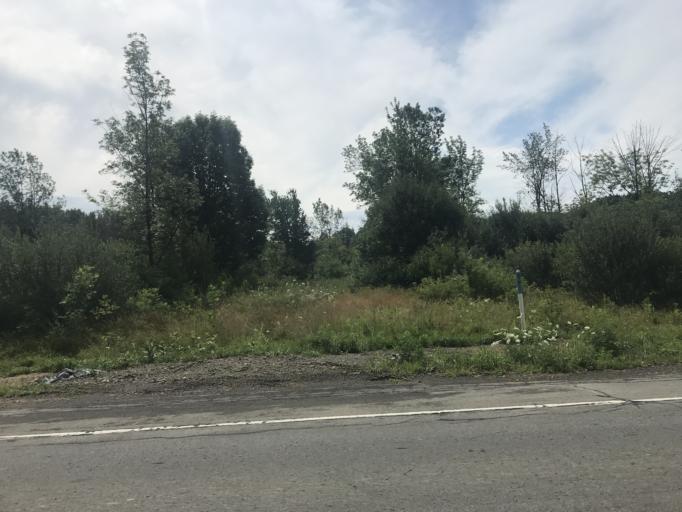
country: US
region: New York
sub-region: Chautauqua County
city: Silver Creek
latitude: 42.5457
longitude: -79.1839
